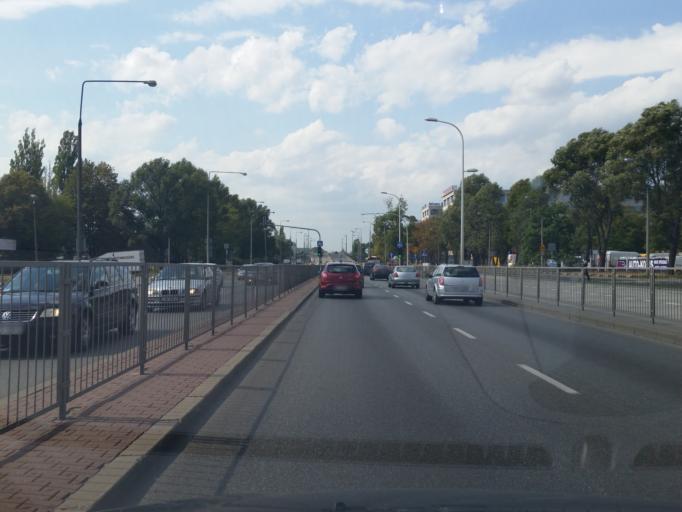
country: PL
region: Masovian Voivodeship
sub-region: Warszawa
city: Wlochy
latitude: 52.1928
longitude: 20.9446
